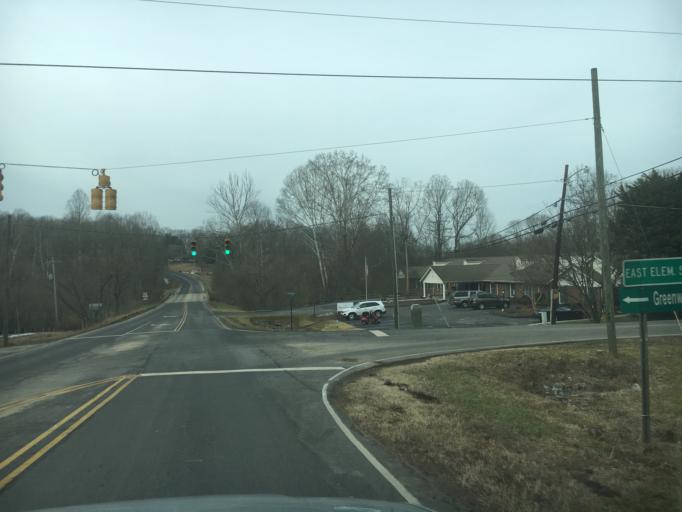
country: US
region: North Carolina
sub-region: Iredell County
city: Statesville
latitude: 35.7968
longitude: -80.8369
